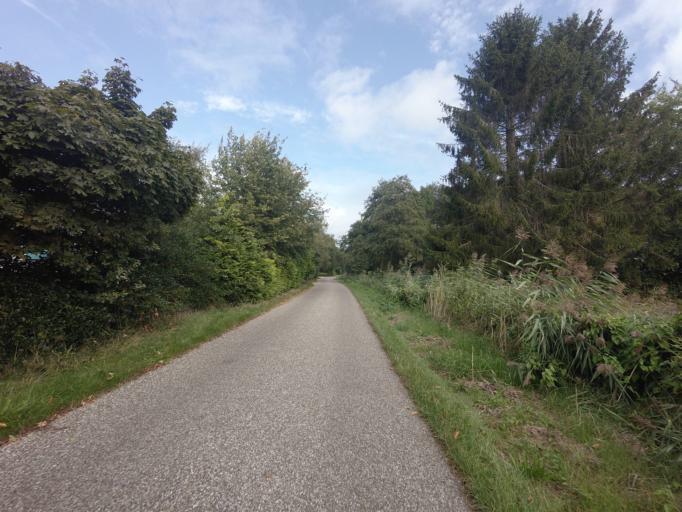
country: NL
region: Friesland
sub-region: Gemeente Heerenveen
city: Jubbega
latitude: 52.9878
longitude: 6.1136
